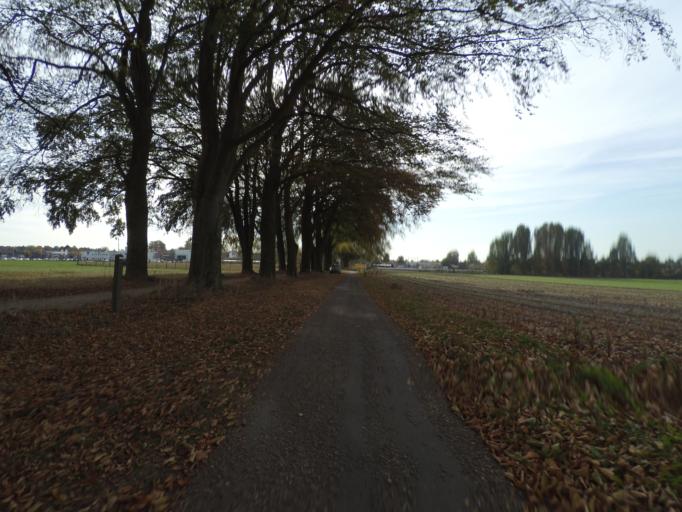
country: NL
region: Overijssel
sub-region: Gemeente Hof van Twente
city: Markelo
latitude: 52.2862
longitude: 6.4217
